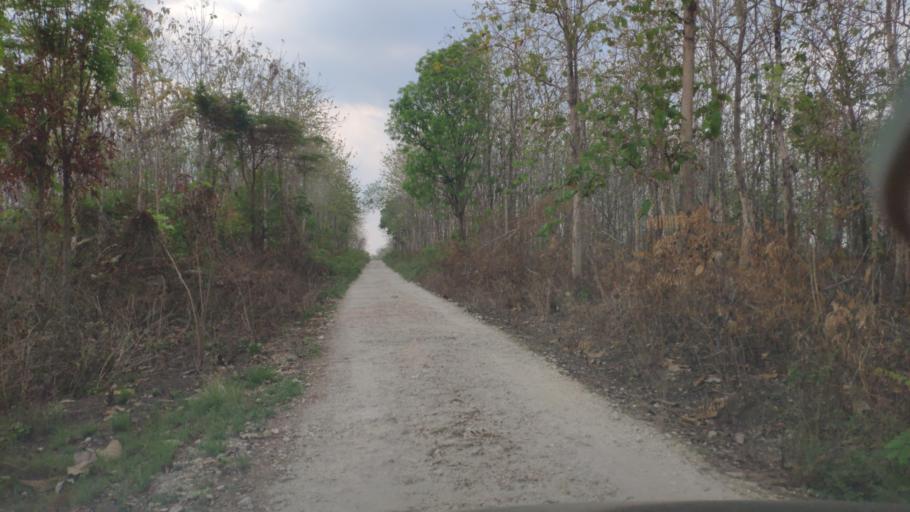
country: ID
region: Central Java
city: Randublatung
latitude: -7.2808
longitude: 111.2889
